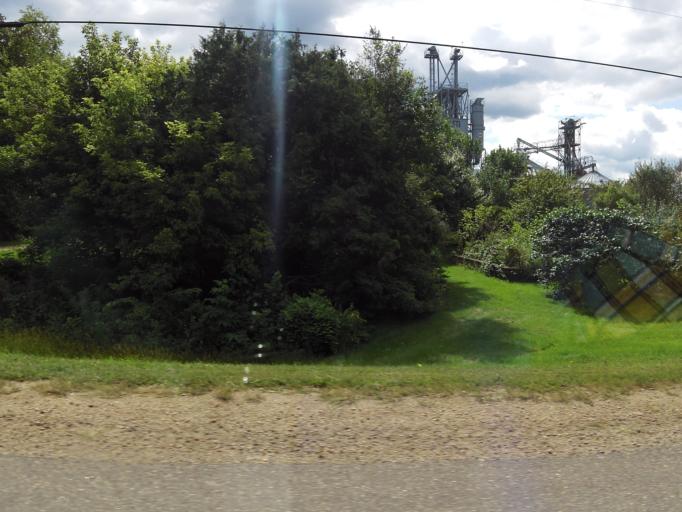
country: US
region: Minnesota
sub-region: Dakota County
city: Rosemount
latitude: 44.7174
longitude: -93.0967
